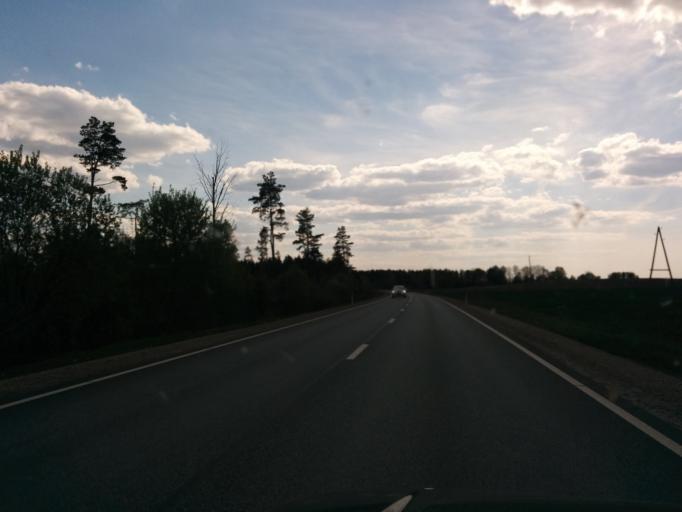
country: LV
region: Krimulda
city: Ragana
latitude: 57.2217
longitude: 24.7926
